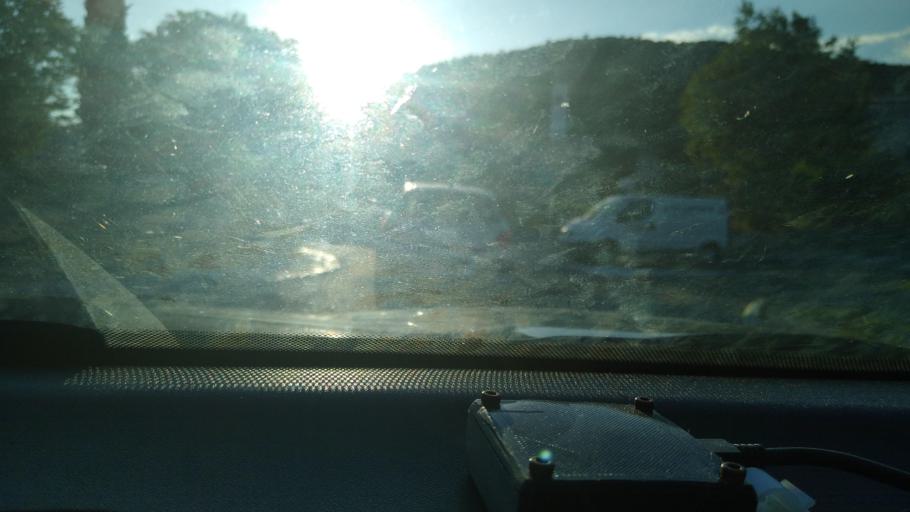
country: FR
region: Languedoc-Roussillon
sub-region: Departement des Pyrenees-Orientales
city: Prades
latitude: 42.6250
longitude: 2.4189
